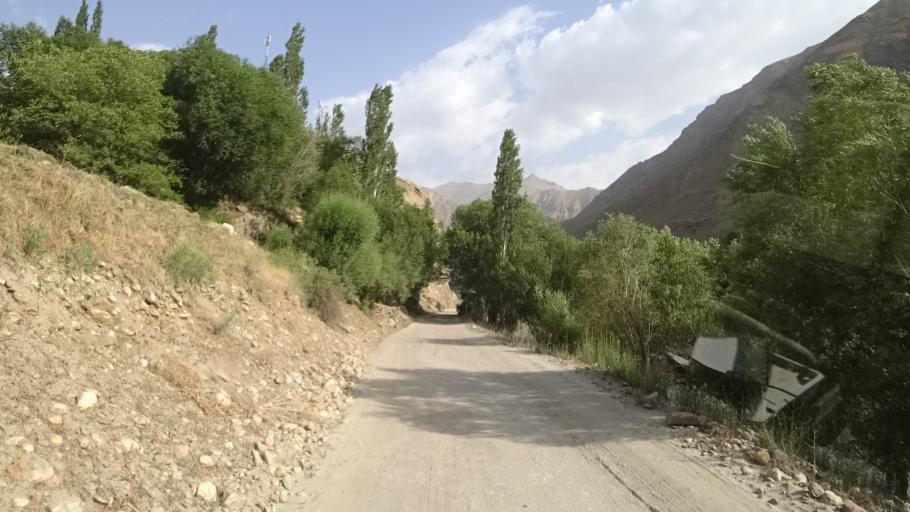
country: TJ
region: Gorno-Badakhshan
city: Khorugh
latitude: 37.3242
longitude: 71.4948
